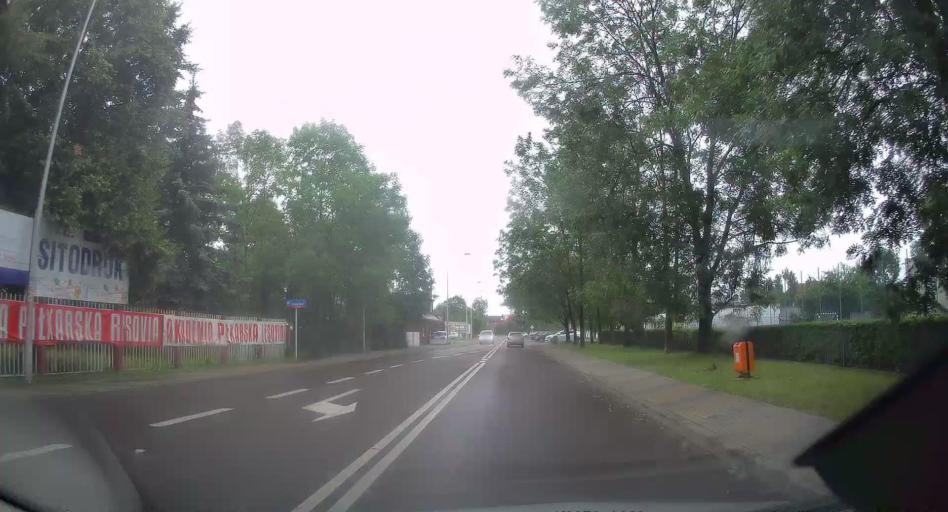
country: PL
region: Subcarpathian Voivodeship
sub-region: Rzeszow
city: Rzeszow
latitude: 50.0388
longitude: 21.9834
